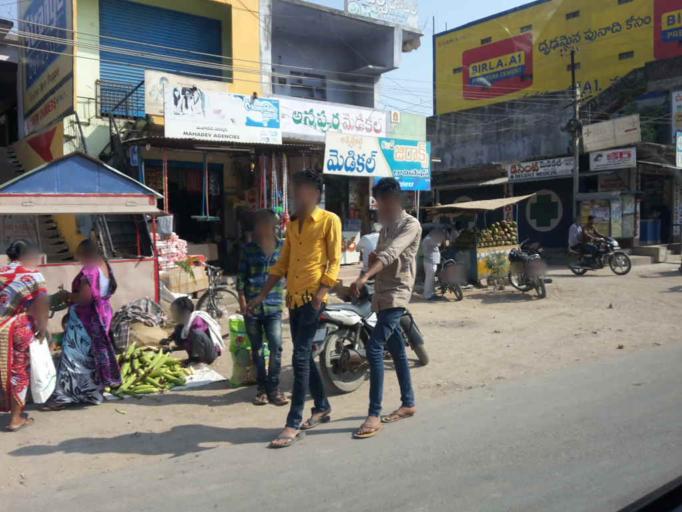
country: IN
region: Telangana
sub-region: Karimnagar
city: Koratla
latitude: 18.8477
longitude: 78.6226
